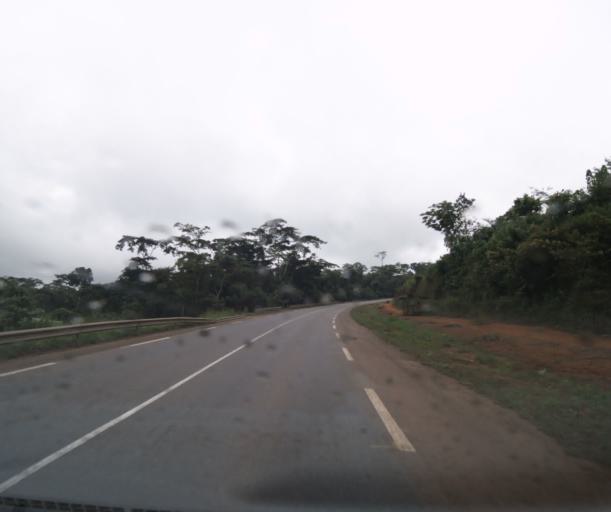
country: CM
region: Centre
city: Mbankomo
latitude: 3.7730
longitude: 11.1566
